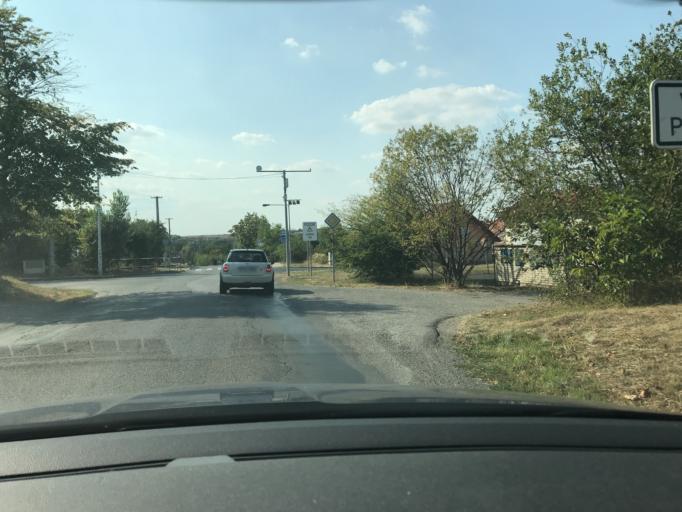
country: CZ
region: Central Bohemia
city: Velke Prilepy
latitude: 50.1572
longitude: 14.3216
